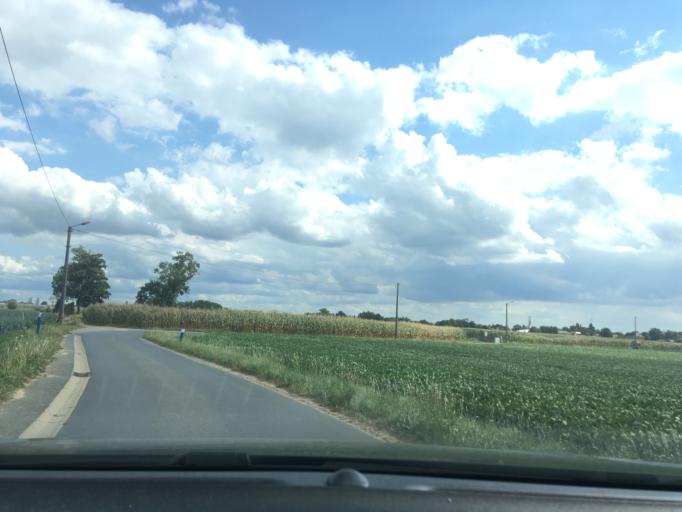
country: BE
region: Flanders
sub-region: Provincie West-Vlaanderen
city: Staden
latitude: 50.9660
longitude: 3.0431
